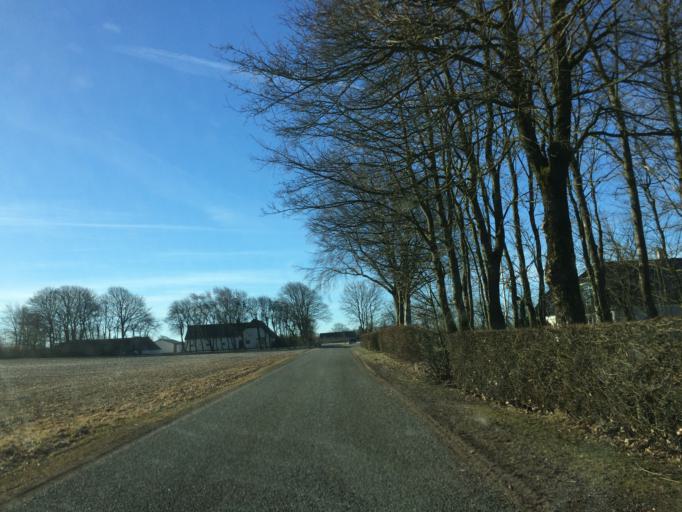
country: DK
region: North Denmark
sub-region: Mariagerfjord Kommune
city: Hobro
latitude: 56.6394
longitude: 9.6425
